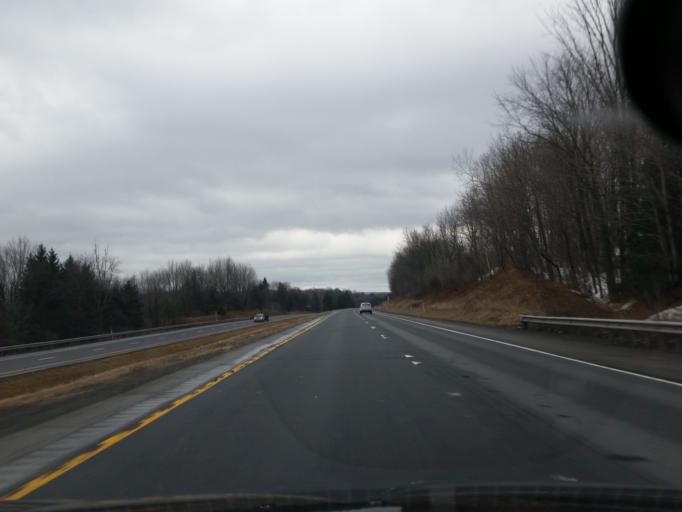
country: US
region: Pennsylvania
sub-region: Lackawanna County
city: Dalton
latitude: 41.6170
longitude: -75.6443
